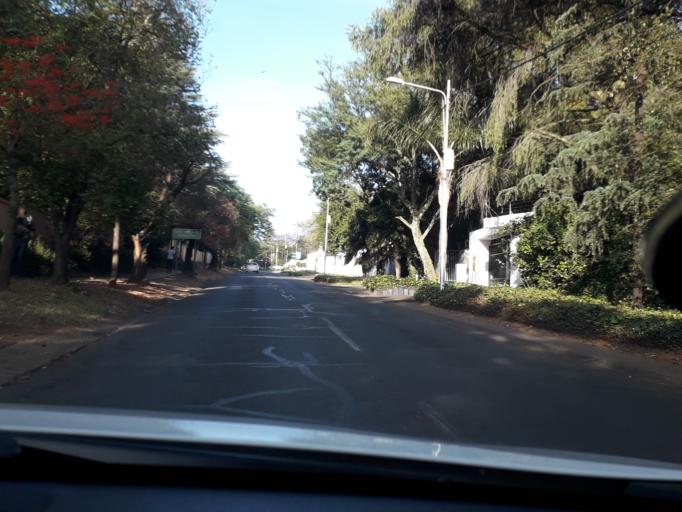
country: ZA
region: Gauteng
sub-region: City of Johannesburg Metropolitan Municipality
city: Johannesburg
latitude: -26.1223
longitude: 28.0615
